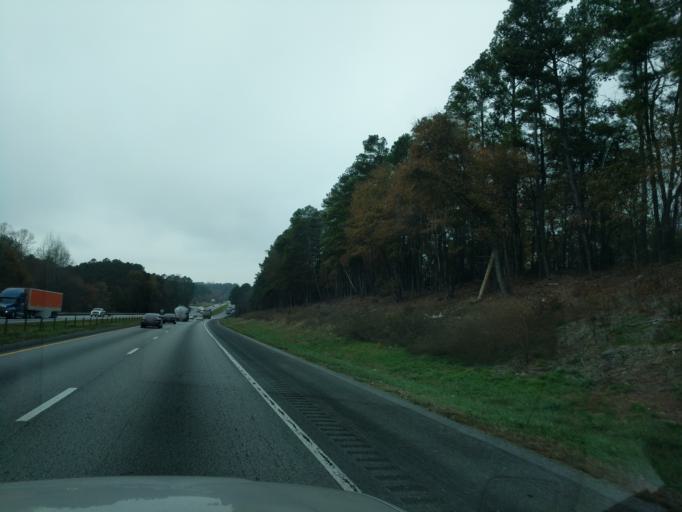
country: US
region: South Carolina
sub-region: Anderson County
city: Northlake
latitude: 34.5717
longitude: -82.7266
